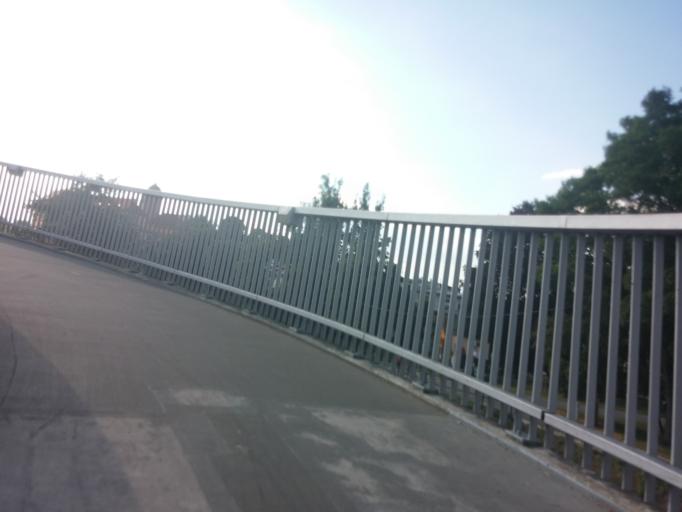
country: CZ
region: Central Bohemia
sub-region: Okres Nymburk
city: Podebrady
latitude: 50.1402
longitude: 15.1230
